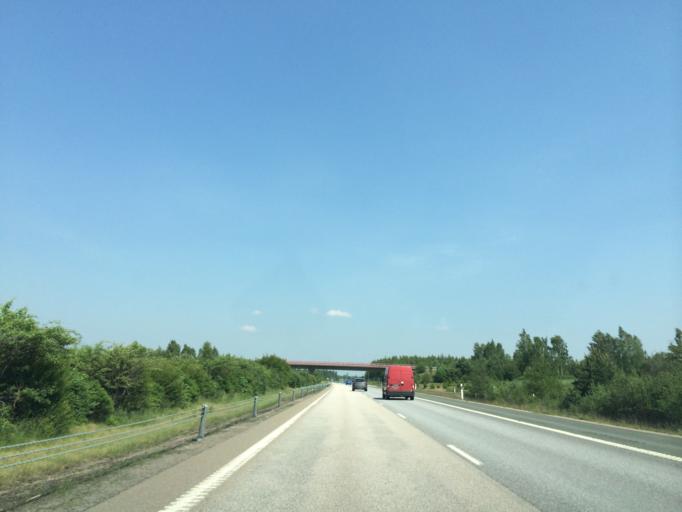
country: SE
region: Kronoberg
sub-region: Ljungby Kommun
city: Lagan
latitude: 57.0371
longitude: 14.0518
